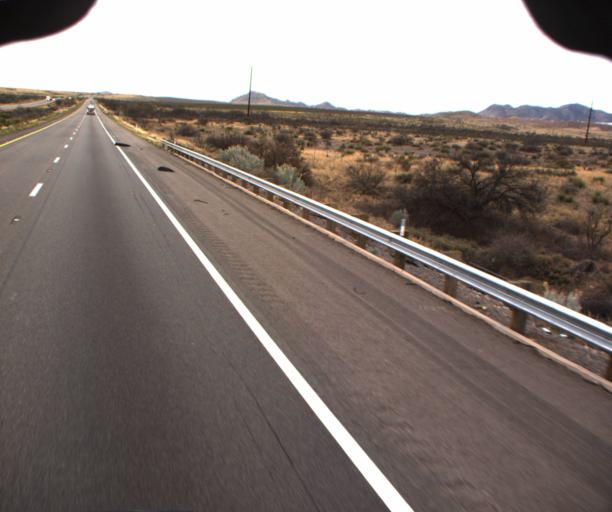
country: US
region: Arizona
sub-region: Cochise County
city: Willcox
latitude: 32.1095
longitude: -110.0250
